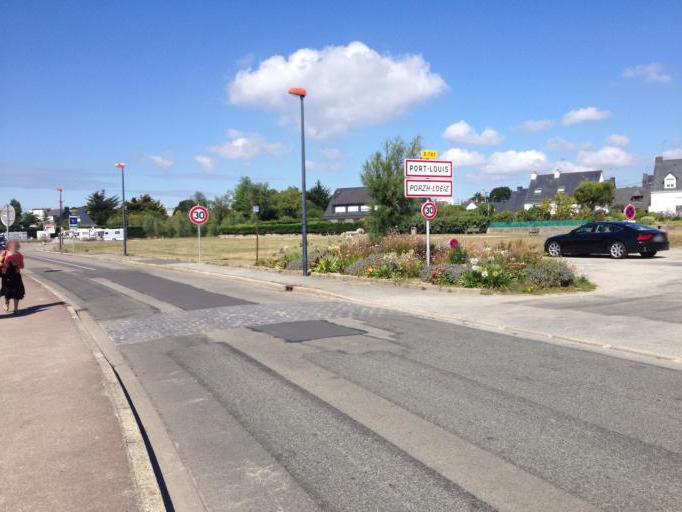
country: FR
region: Brittany
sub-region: Departement du Morbihan
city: Port-Louis
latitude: 47.7089
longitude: -3.3411
